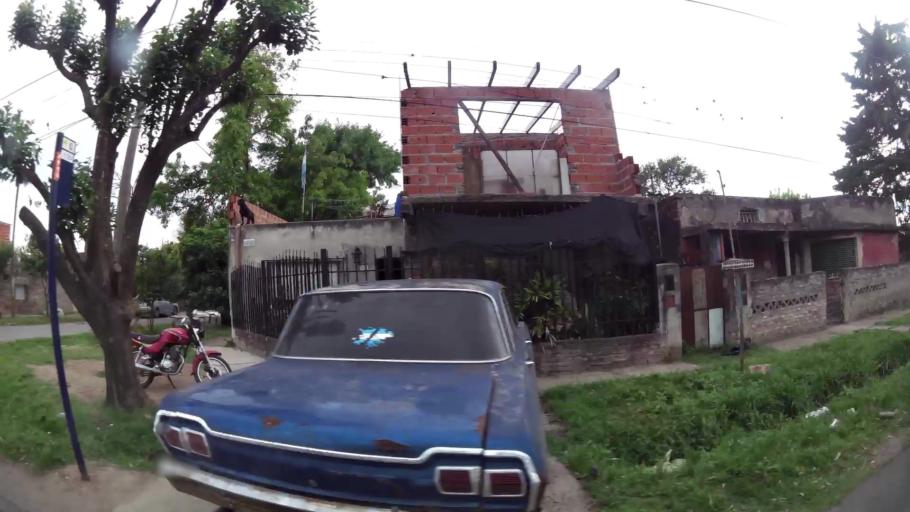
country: AR
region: Santa Fe
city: Gobernador Galvez
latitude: -32.9983
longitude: -60.6852
